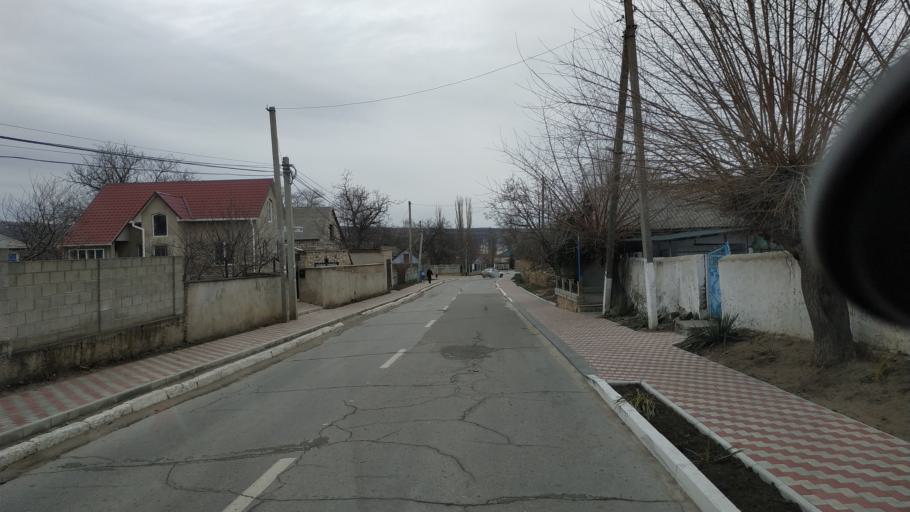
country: MD
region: Telenesti
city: Cocieri
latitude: 47.3450
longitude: 29.0919
